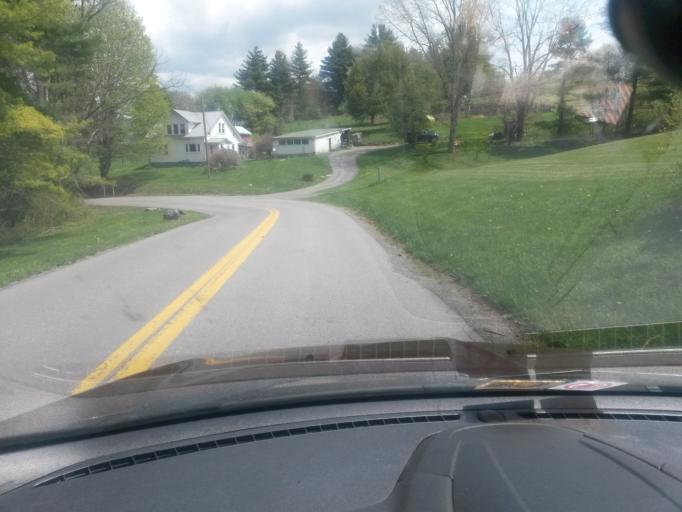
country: US
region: West Virginia
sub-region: Pocahontas County
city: Marlinton
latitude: 38.1319
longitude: -80.2100
